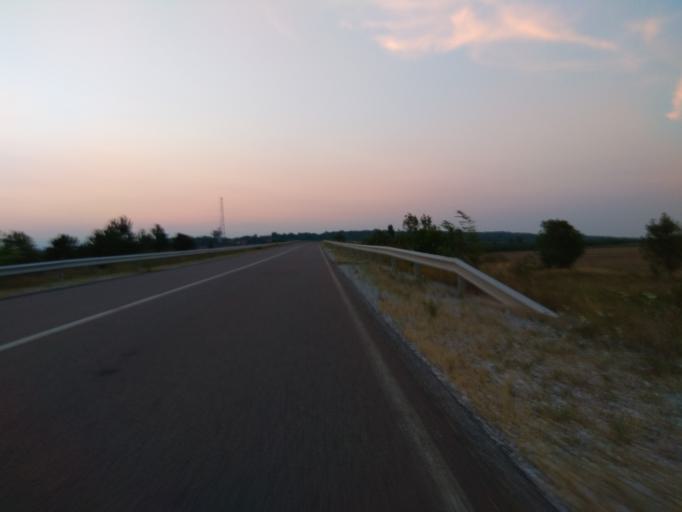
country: HU
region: Borsod-Abauj-Zemplen
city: Emod
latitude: 47.9327
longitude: 20.8294
